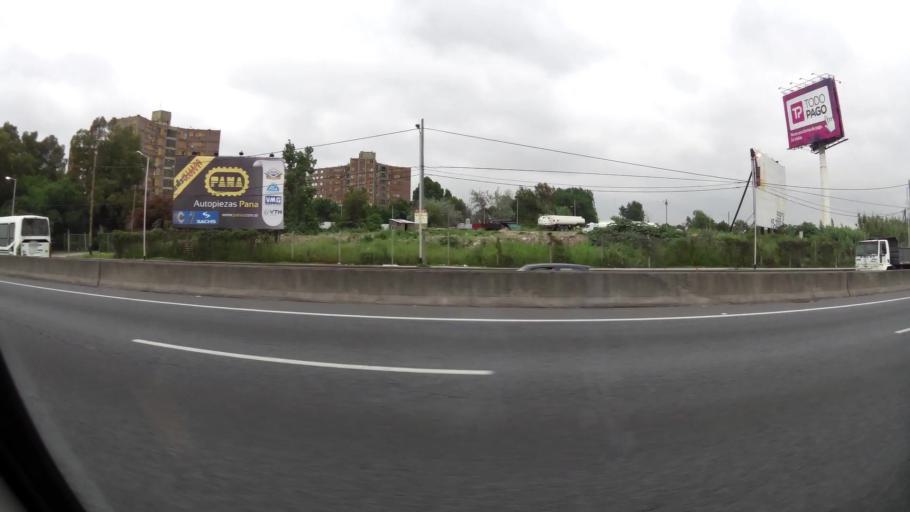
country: AR
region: Buenos Aires
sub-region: Partido de Avellaneda
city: Avellaneda
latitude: -34.6711
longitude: -58.3372
